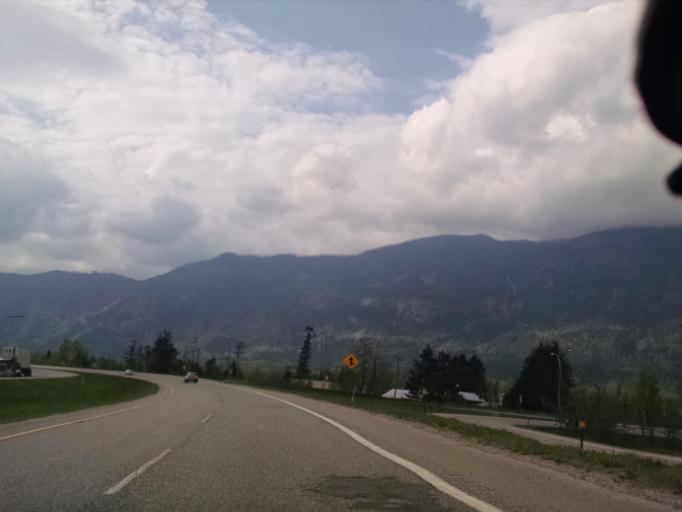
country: CA
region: British Columbia
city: Hope
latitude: 49.3643
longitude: -121.5212
